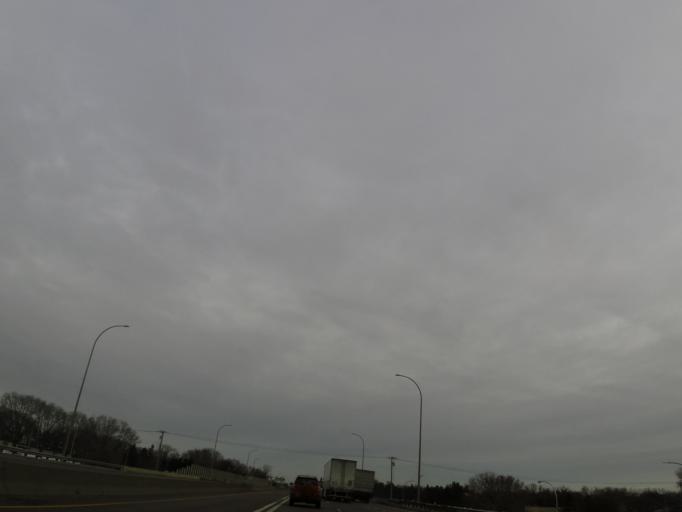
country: US
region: Minnesota
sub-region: Hennepin County
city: Bloomington
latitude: 44.8110
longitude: -93.2916
